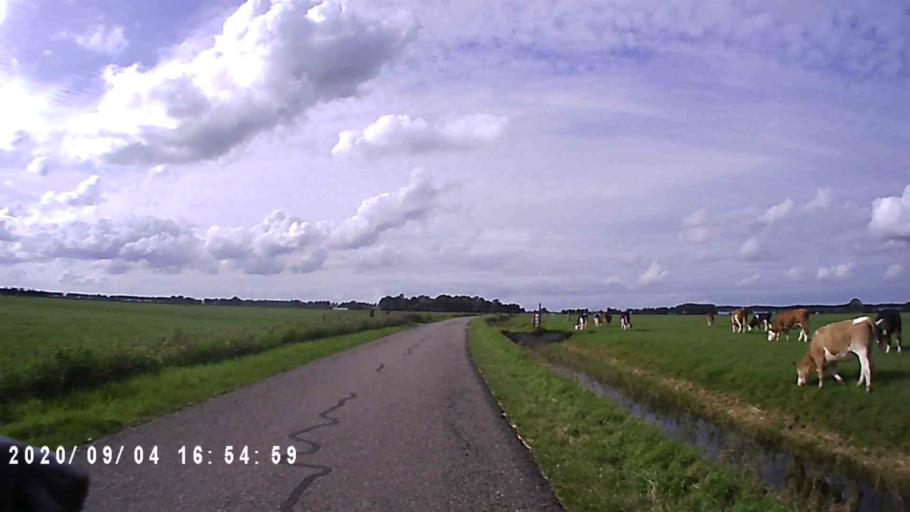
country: NL
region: Groningen
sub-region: Gemeente Groningen
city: Korrewegwijk
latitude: 53.2623
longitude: 6.5205
